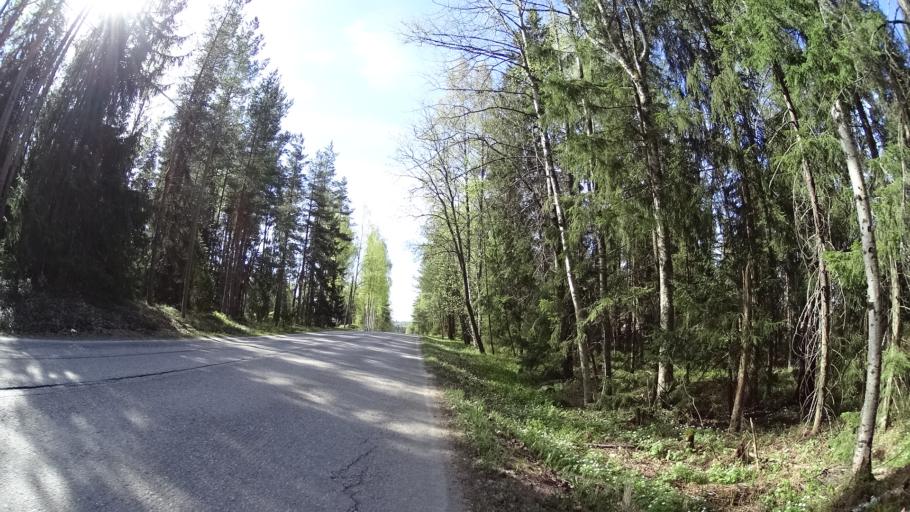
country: FI
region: Uusimaa
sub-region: Helsinki
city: Nurmijaervi
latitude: 60.4412
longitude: 24.8301
